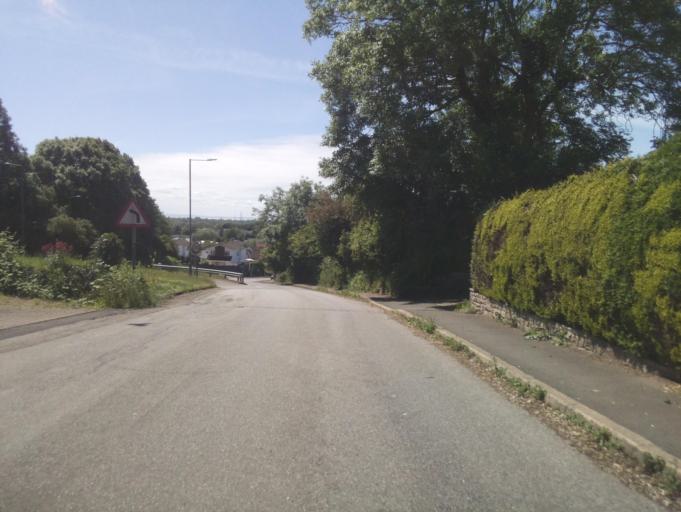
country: GB
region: Wales
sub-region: Monmouthshire
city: Magor
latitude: 51.5845
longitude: -2.8272
